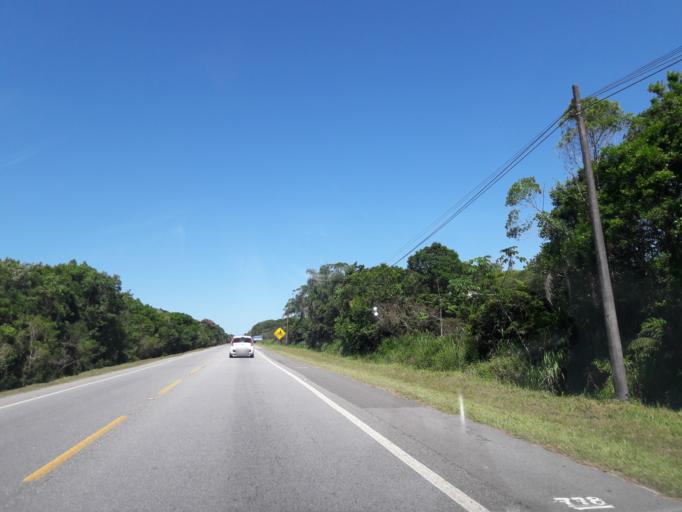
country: BR
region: Parana
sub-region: Pontal Do Parana
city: Pontal do Parana
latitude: -25.6796
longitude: -48.5018
